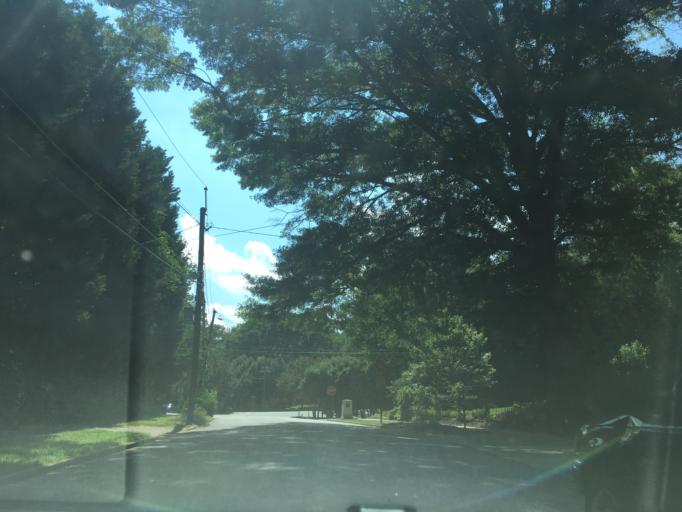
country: US
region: Georgia
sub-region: DeKalb County
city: Druid Hills
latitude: 33.8021
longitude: -84.3634
